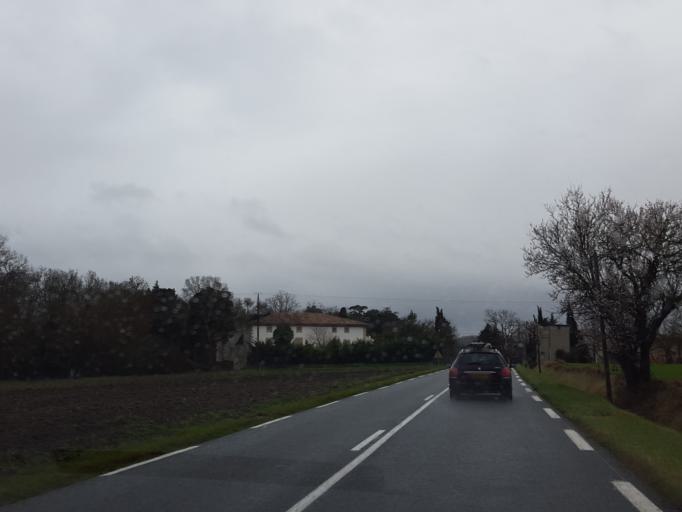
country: FR
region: Languedoc-Roussillon
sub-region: Departement de l'Aude
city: Bram
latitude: 43.2118
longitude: 2.0703
